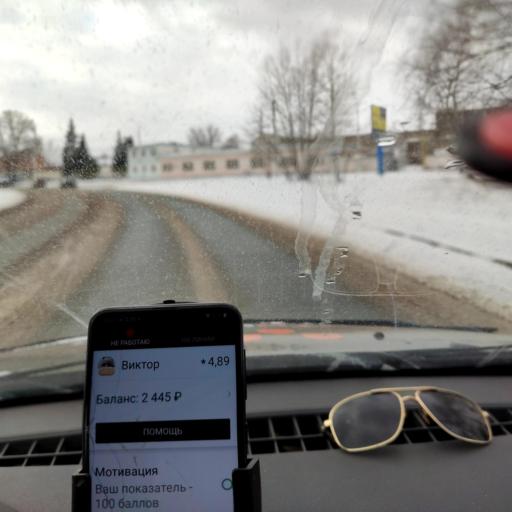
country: RU
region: Bashkortostan
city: Ufa
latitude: 54.8265
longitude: 56.1189
